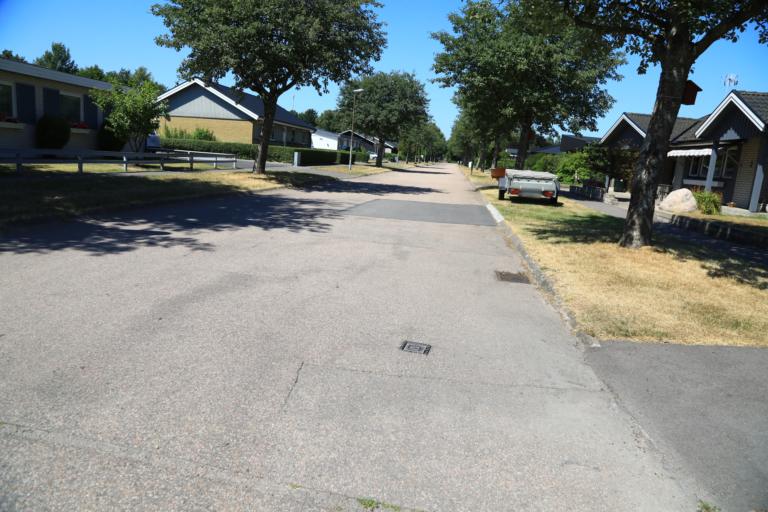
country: SE
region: Halland
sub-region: Halmstads Kommun
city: Fyllinge
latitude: 56.6640
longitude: 12.9114
